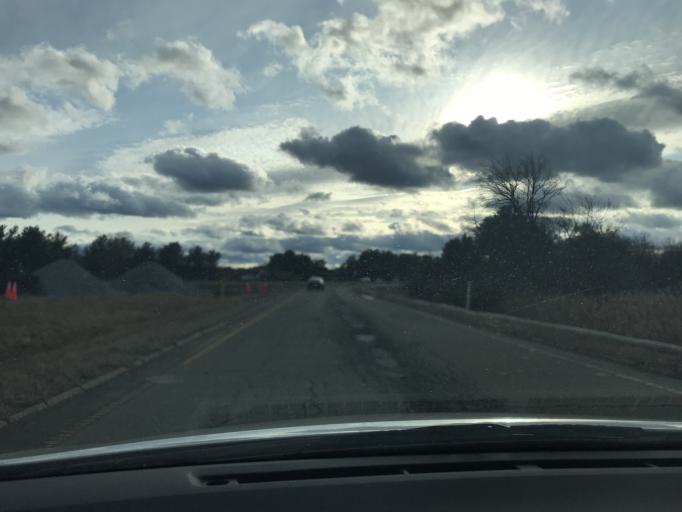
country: US
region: Massachusetts
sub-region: Middlesex County
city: Littleton Common
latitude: 42.5491
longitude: -71.4819
